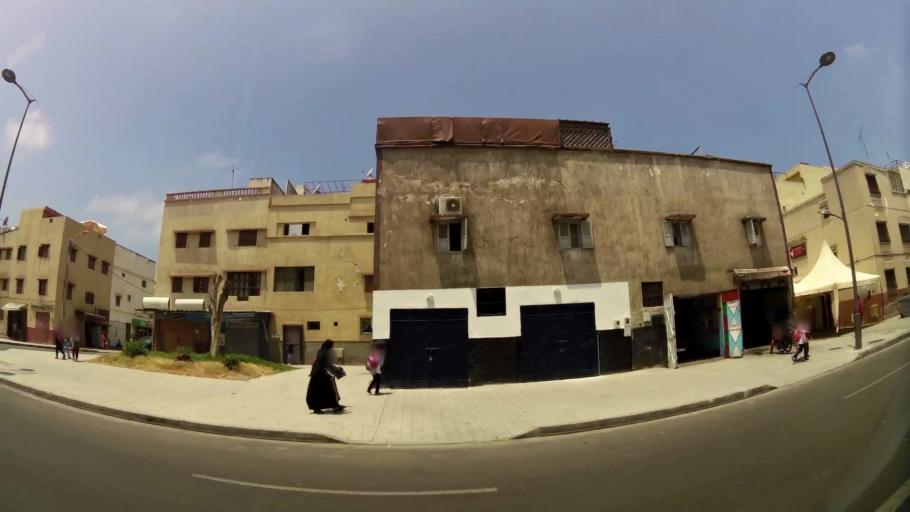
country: MA
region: Rabat-Sale-Zemmour-Zaer
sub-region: Rabat
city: Rabat
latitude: 33.9879
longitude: -6.8753
